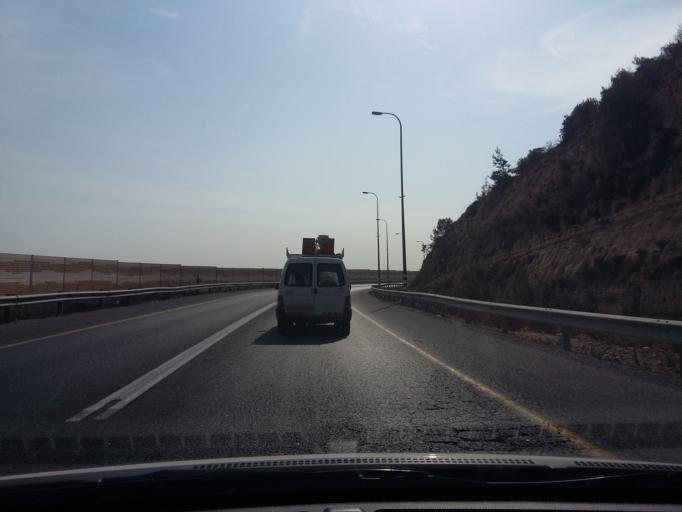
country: PS
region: West Bank
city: Al Khadir
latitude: 31.6934
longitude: 35.1592
